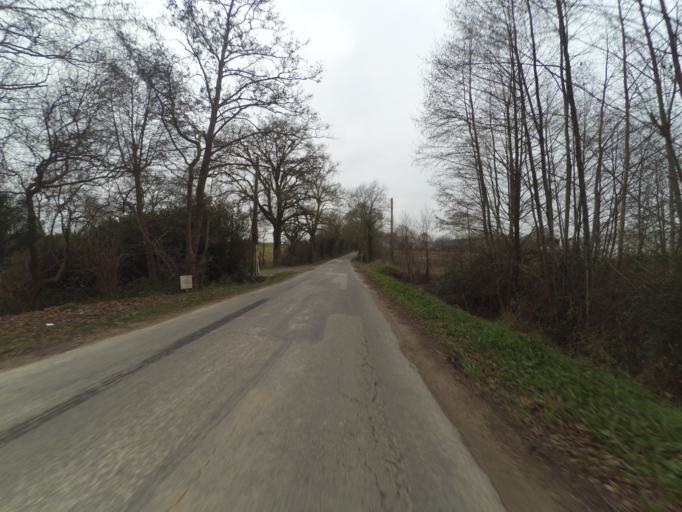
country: FR
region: Pays de la Loire
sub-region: Departement de la Loire-Atlantique
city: Sautron
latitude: 47.2606
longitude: -1.7049
